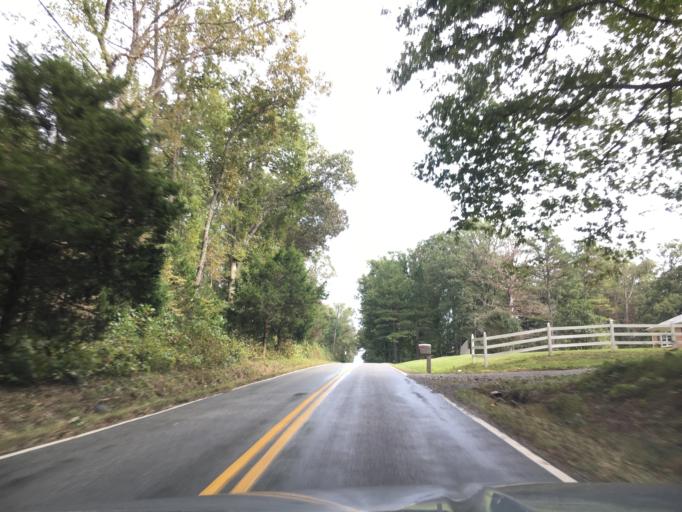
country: US
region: Virginia
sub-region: Goochland County
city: Goochland
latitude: 37.7174
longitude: -77.8316
